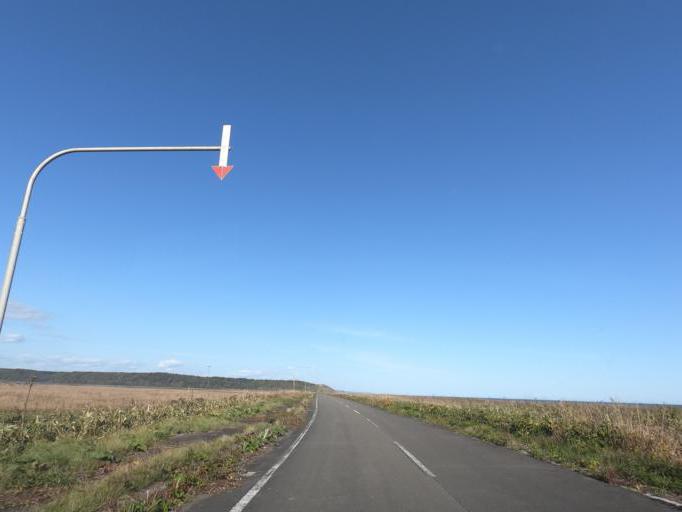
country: JP
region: Hokkaido
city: Obihiro
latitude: 42.5903
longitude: 143.5400
